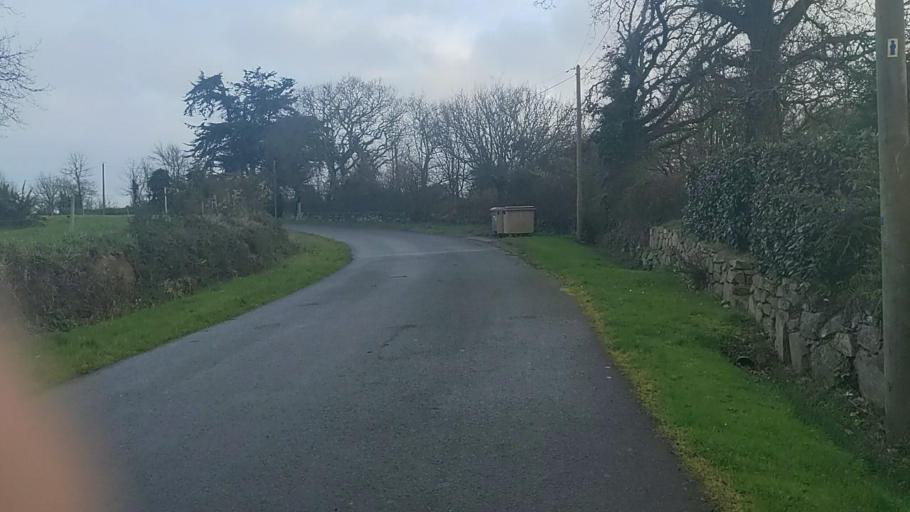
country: FR
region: Brittany
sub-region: Departement des Cotes-d'Armor
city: Plougrescant
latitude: 48.8330
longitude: -3.1870
